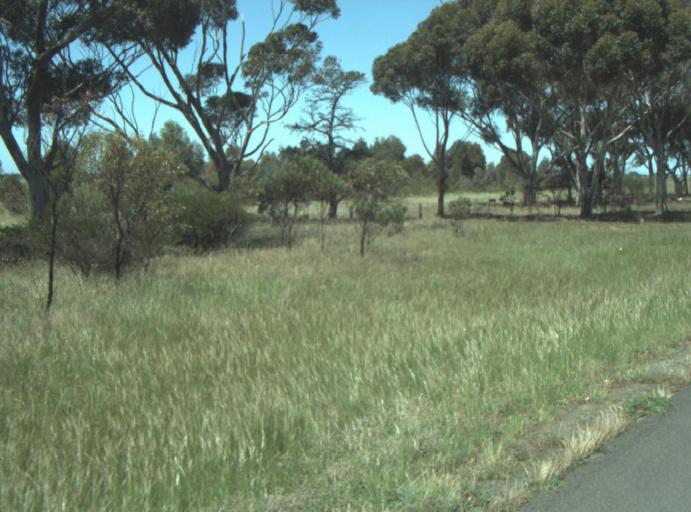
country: AU
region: Victoria
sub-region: Greater Geelong
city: Lara
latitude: -37.9467
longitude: 144.3554
